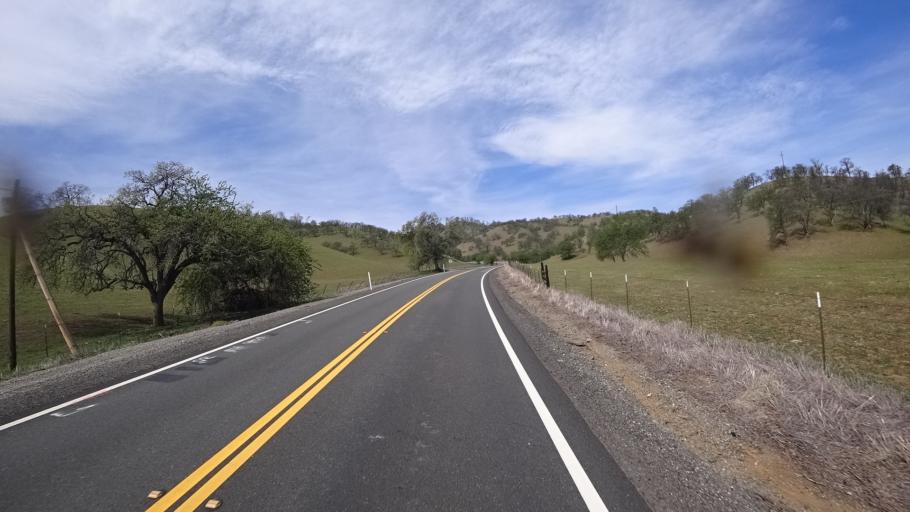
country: US
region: California
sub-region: Glenn County
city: Willows
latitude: 39.5967
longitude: -122.4919
